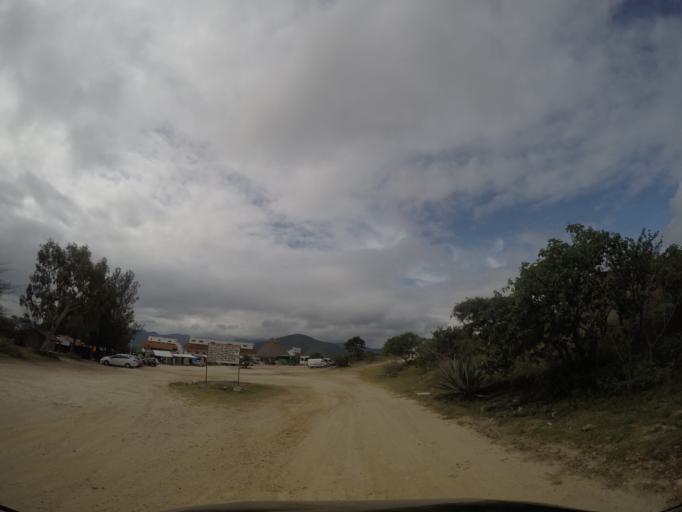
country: MX
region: Oaxaca
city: San Lorenzo Albarradas
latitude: 16.8688
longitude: -96.2766
